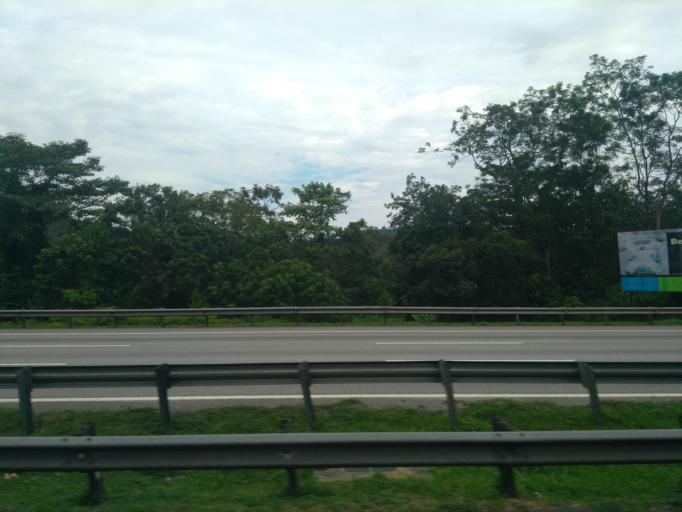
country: MY
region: Negeri Sembilan
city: Tampin
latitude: 2.4665
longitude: 102.1459
